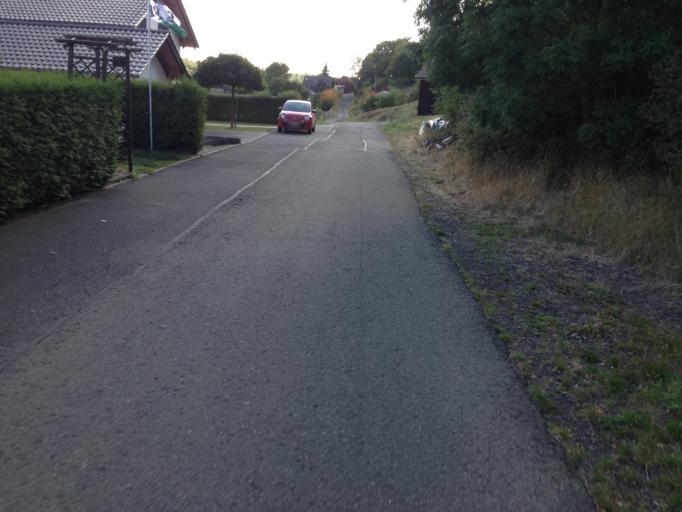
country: DE
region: Hesse
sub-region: Regierungsbezirk Giessen
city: Reiskirchen
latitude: 50.6197
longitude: 8.8529
